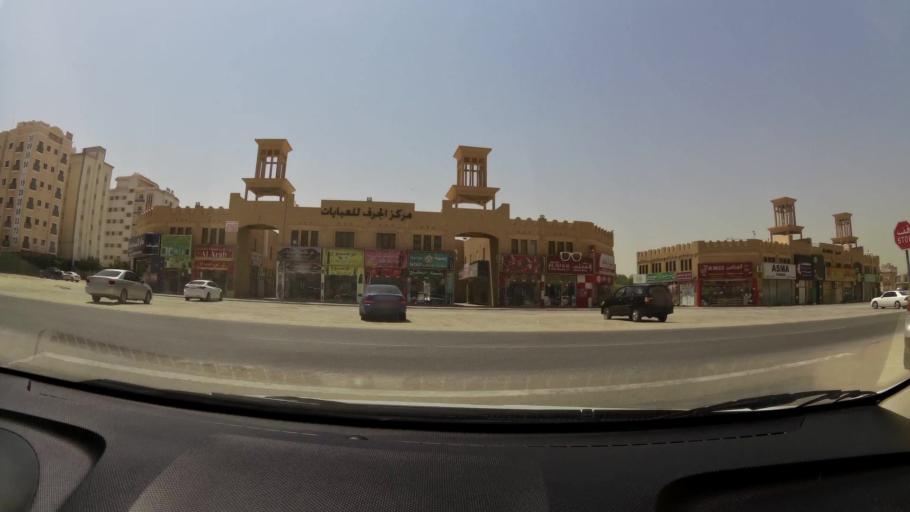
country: AE
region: Ajman
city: Ajman
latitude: 25.4063
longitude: 55.5116
